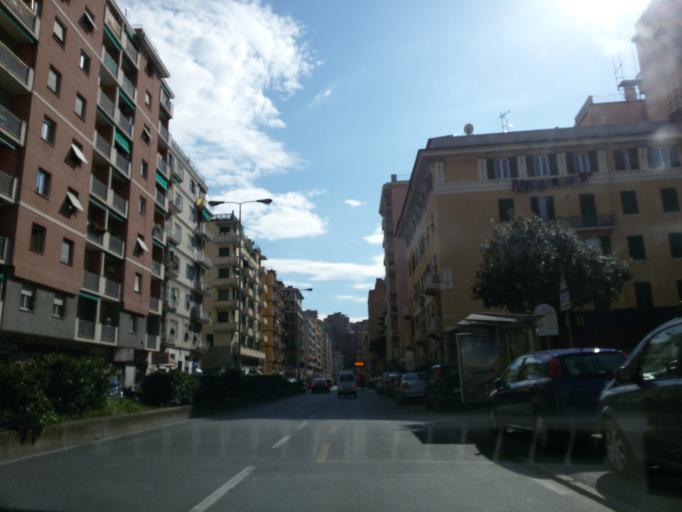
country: IT
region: Liguria
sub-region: Provincia di Genova
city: Genoa
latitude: 44.4181
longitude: 8.9525
